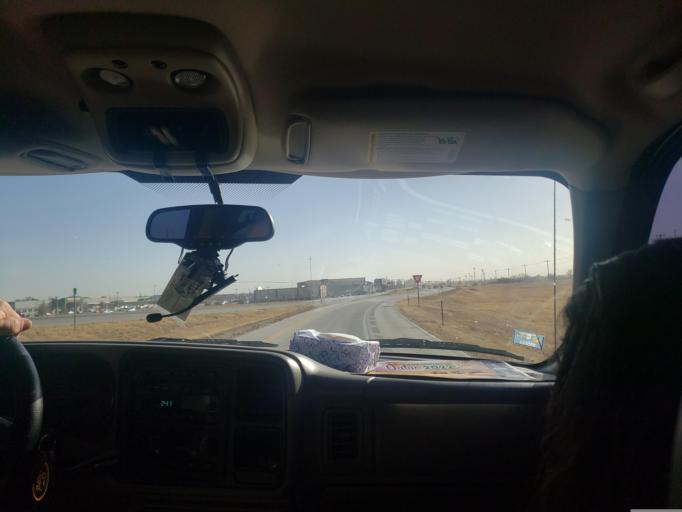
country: US
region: Kansas
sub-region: Finney County
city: Garden City
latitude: 37.9799
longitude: -100.8384
